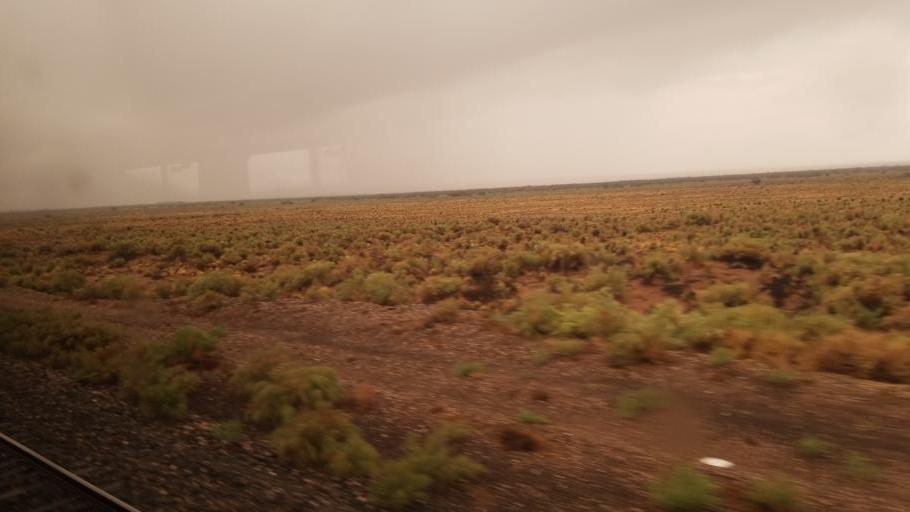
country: US
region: Arizona
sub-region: Navajo County
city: Joseph City
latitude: 34.9675
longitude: -110.4981
